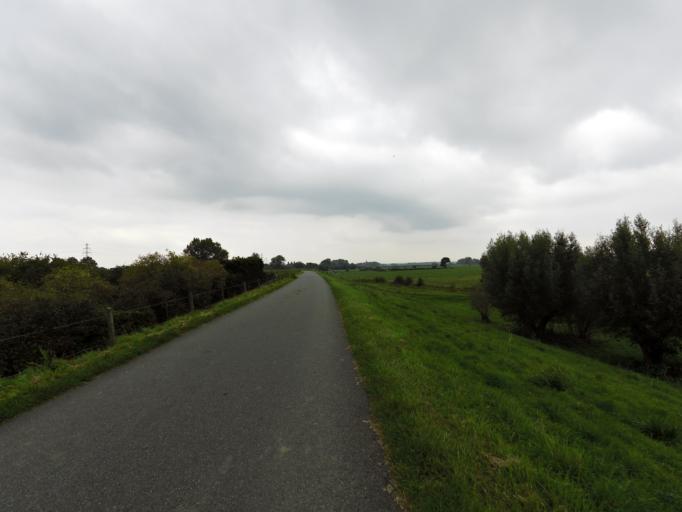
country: NL
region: Gelderland
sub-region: Gemeente Zevenaar
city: Zevenaar
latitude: 51.9136
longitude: 6.0554
